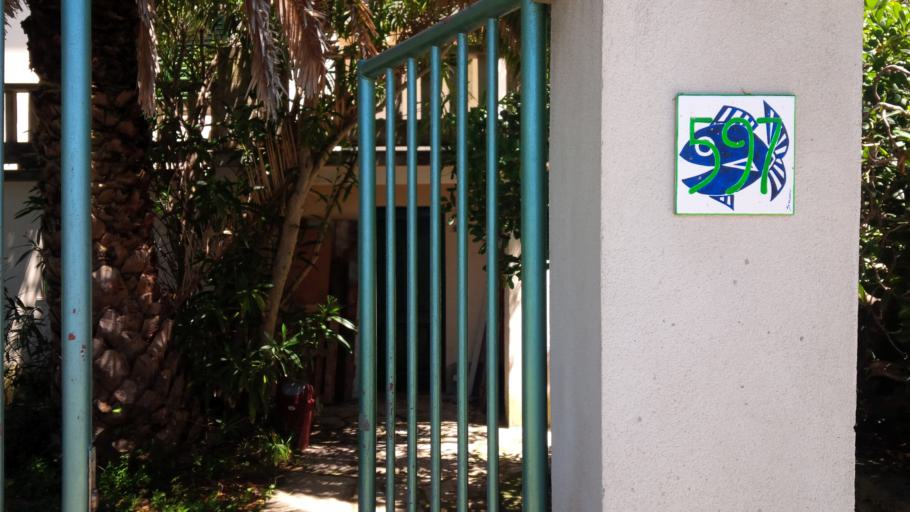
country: HR
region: Licko-Senjska
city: Novalja
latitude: 44.3783
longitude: 14.6911
